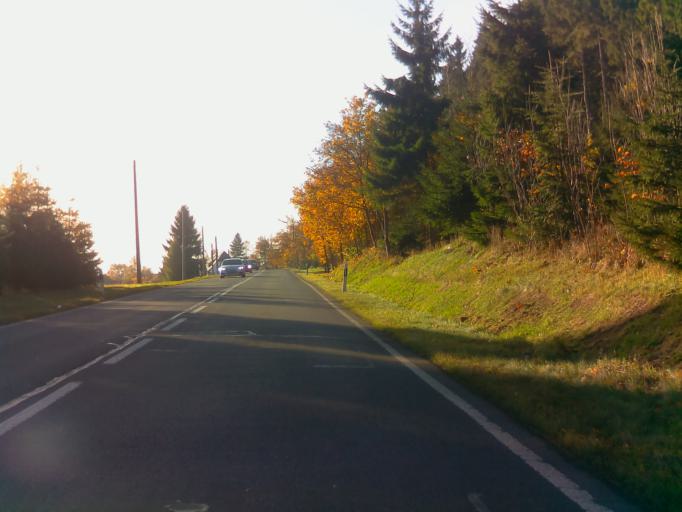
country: DE
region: Thuringia
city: Reichmannsdorf
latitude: 50.5576
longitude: 11.2584
